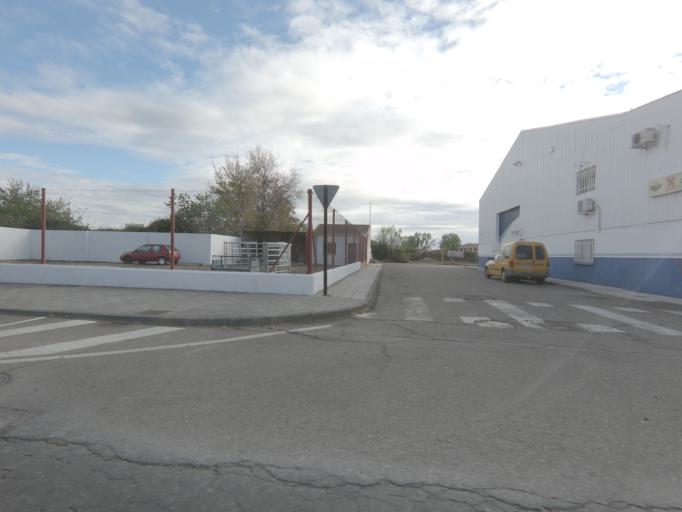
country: ES
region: Extremadura
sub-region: Provincia de Caceres
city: Moraleja
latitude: 40.0732
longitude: -6.6608
